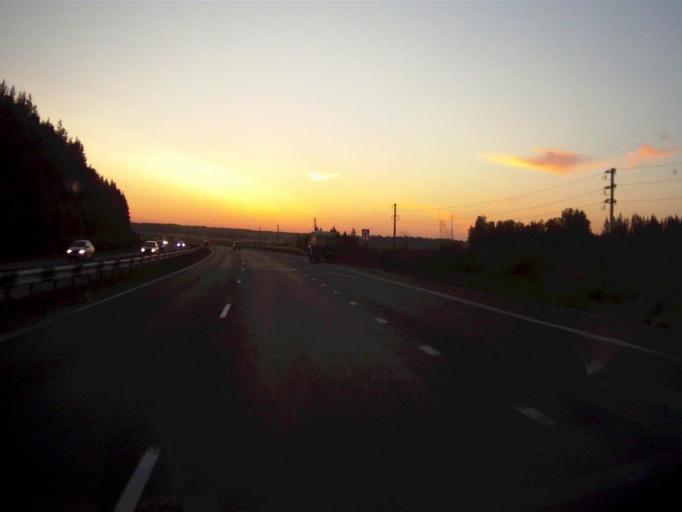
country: RU
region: Chelyabinsk
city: Roshchino
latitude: 55.1941
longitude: 61.2147
